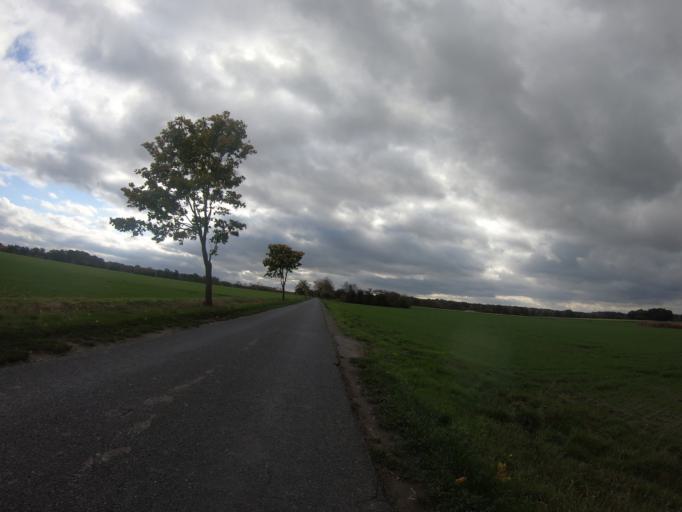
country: DE
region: Lower Saxony
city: Ribbesbuttel
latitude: 52.4218
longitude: 10.4832
